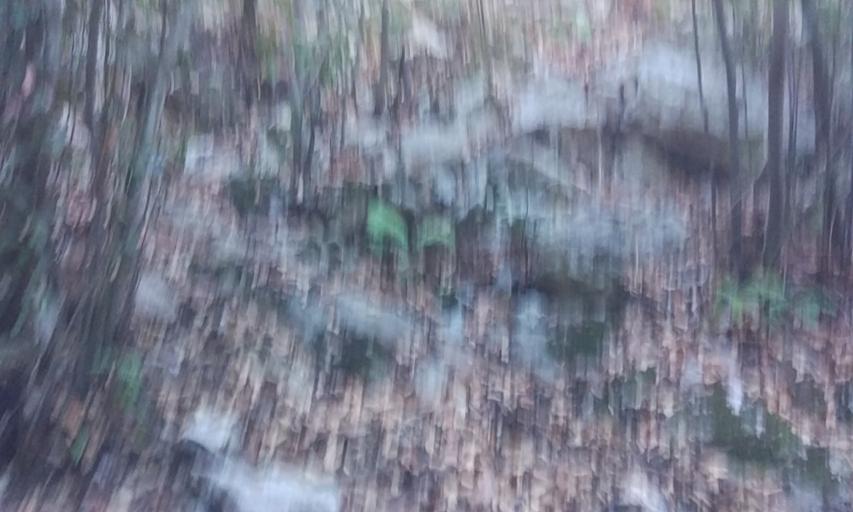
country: TR
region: Antalya
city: Tekirova
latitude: 36.3798
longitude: 30.4766
